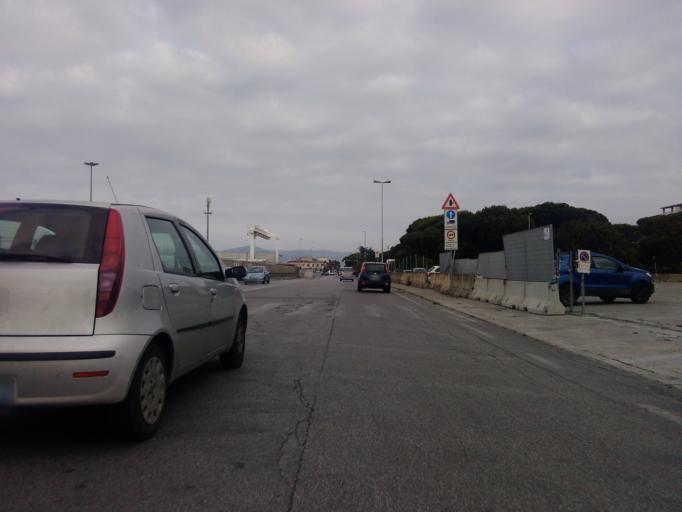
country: IT
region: Tuscany
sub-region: Provincia di Massa-Carrara
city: Marina di Carrara
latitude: 44.0350
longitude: 10.0464
